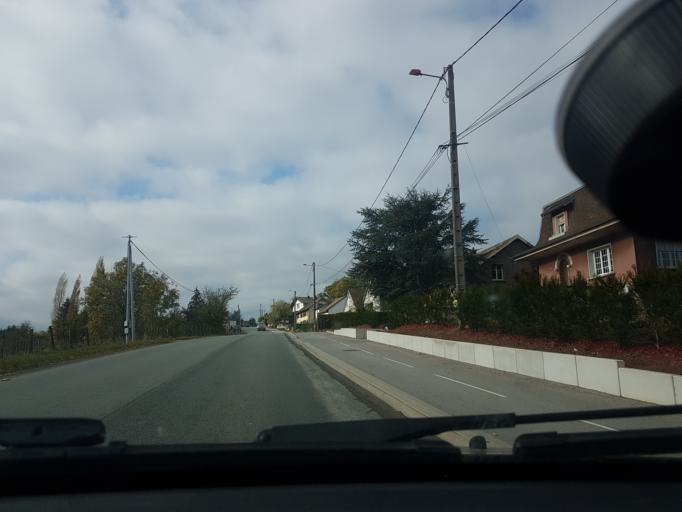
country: FR
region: Franche-Comte
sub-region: Departement de la Haute-Saone
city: Chalonvillars
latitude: 47.6427
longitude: 6.7911
